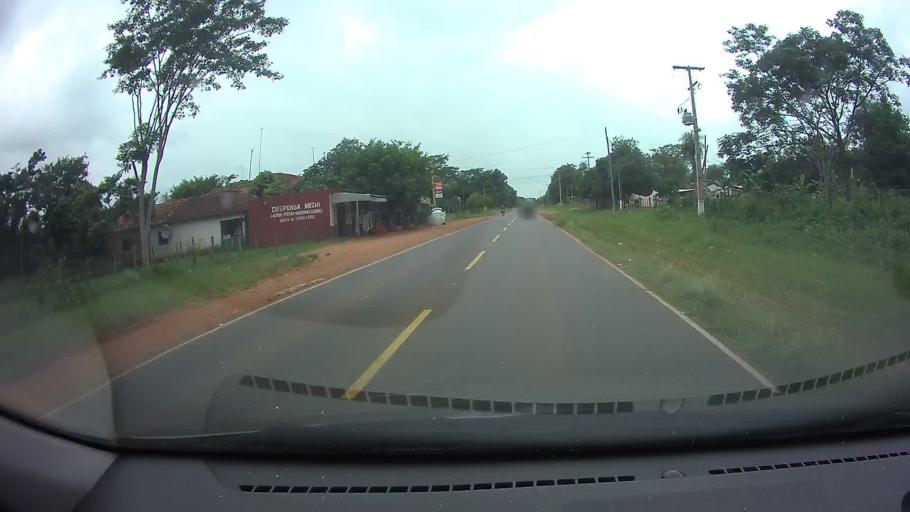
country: PY
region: Paraguari
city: Carapegua
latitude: -25.7520
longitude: -57.2624
